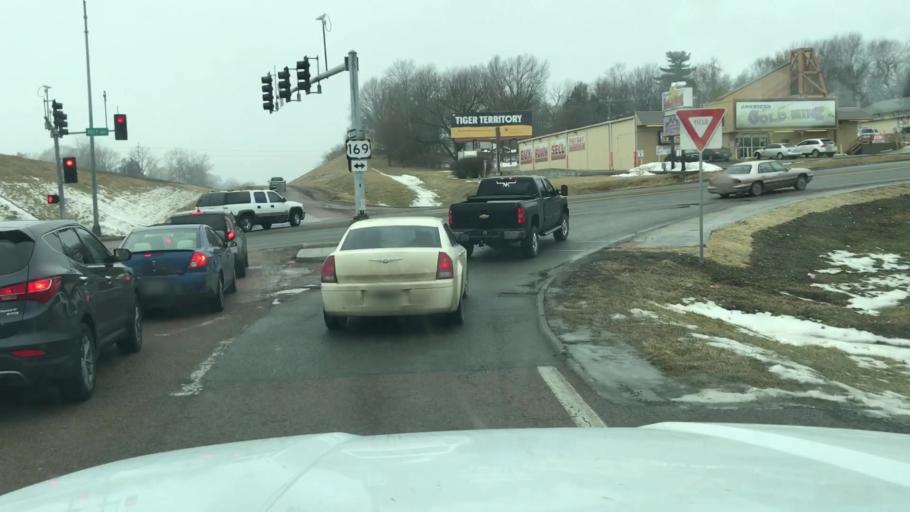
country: US
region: Missouri
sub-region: Buchanan County
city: Saint Joseph
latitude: 39.7473
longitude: -94.8018
